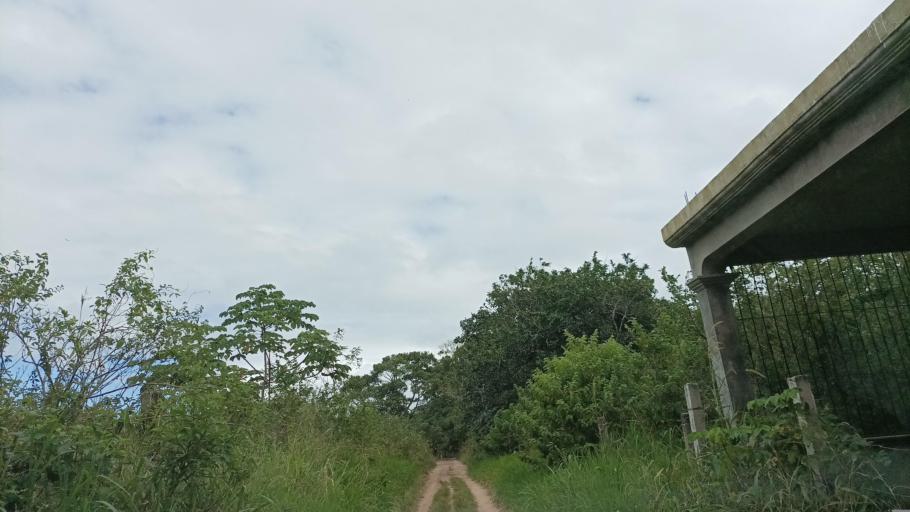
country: MX
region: Veracruz
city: Minatitlan
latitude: 18.0422
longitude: -94.5594
